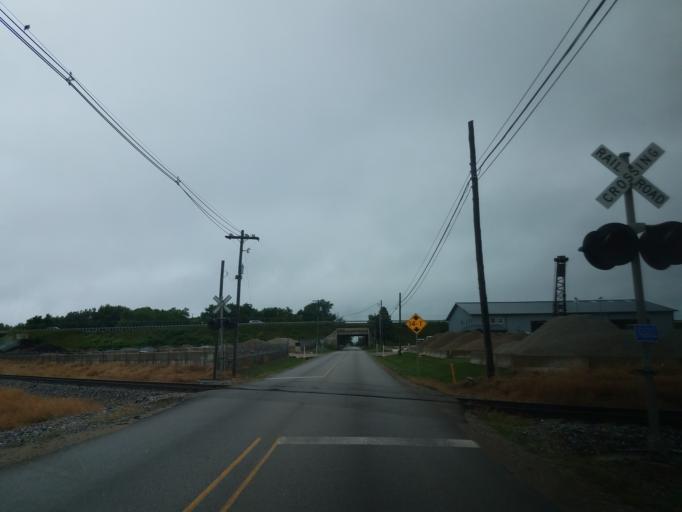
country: US
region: Illinois
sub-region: McLean County
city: Bloomington
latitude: 40.4580
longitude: -88.9815
